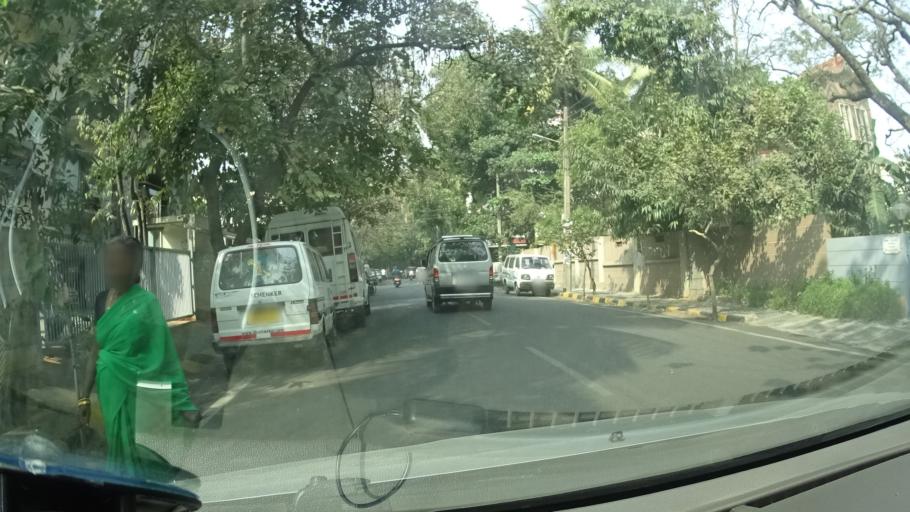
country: IN
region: Karnataka
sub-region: Bangalore Urban
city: Bangalore
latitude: 13.0019
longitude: 77.5673
